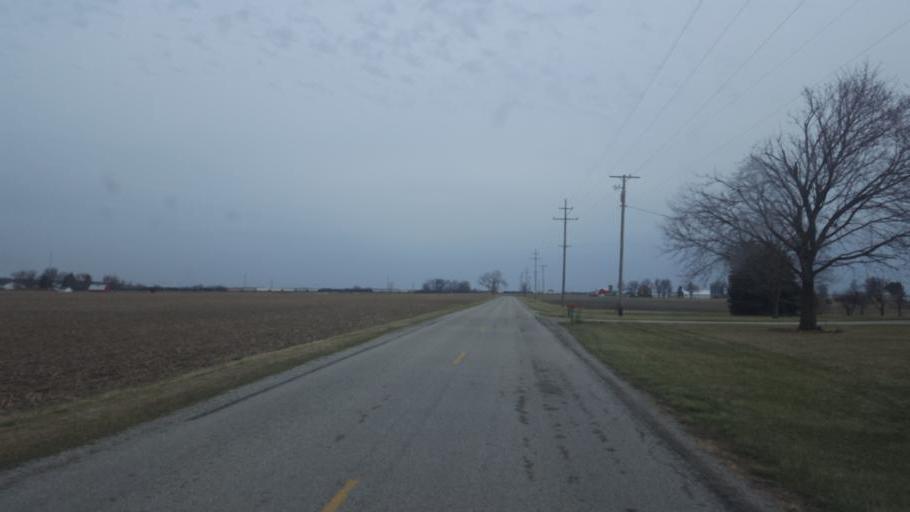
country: US
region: Ohio
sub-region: Marion County
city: Marion
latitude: 40.6684
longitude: -83.0732
